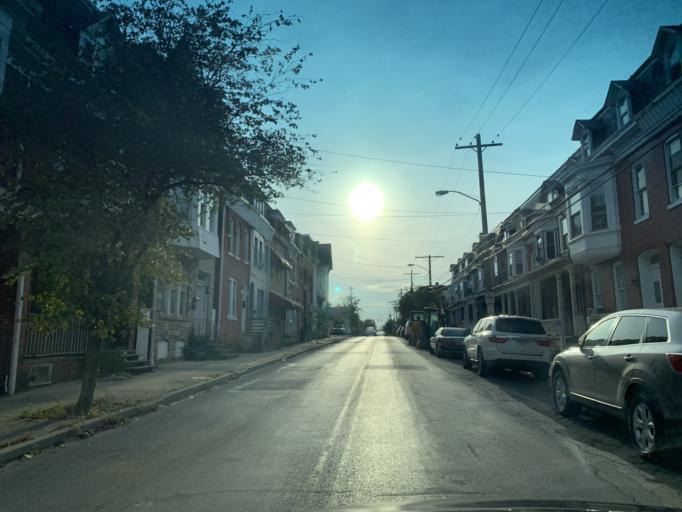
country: US
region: Pennsylvania
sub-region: York County
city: York
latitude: 39.9601
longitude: -76.7198
